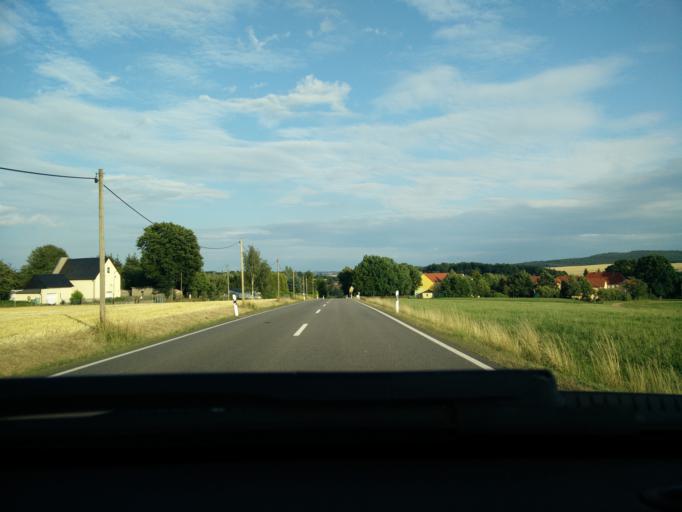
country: DE
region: Saxony
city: Konigsfeld
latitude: 51.0665
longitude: 12.7513
